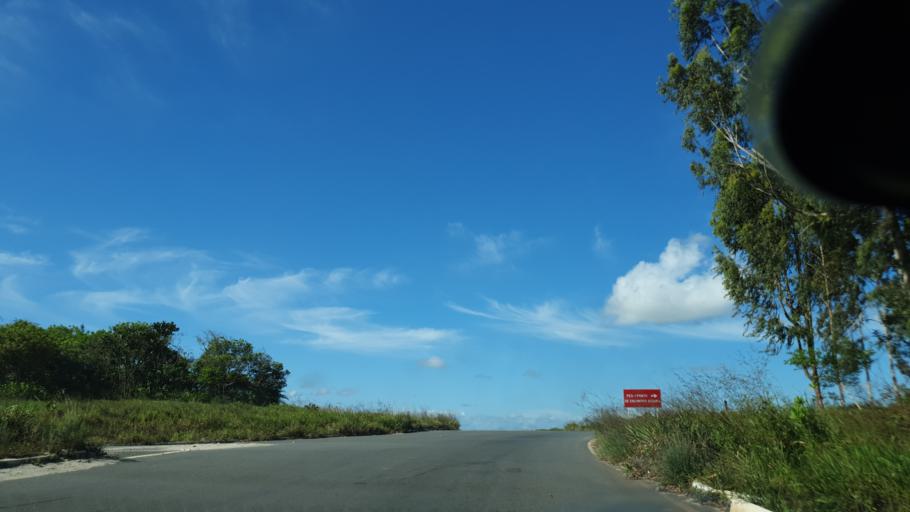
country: BR
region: Bahia
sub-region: Camacari
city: Camacari
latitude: -12.6808
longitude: -38.2817
